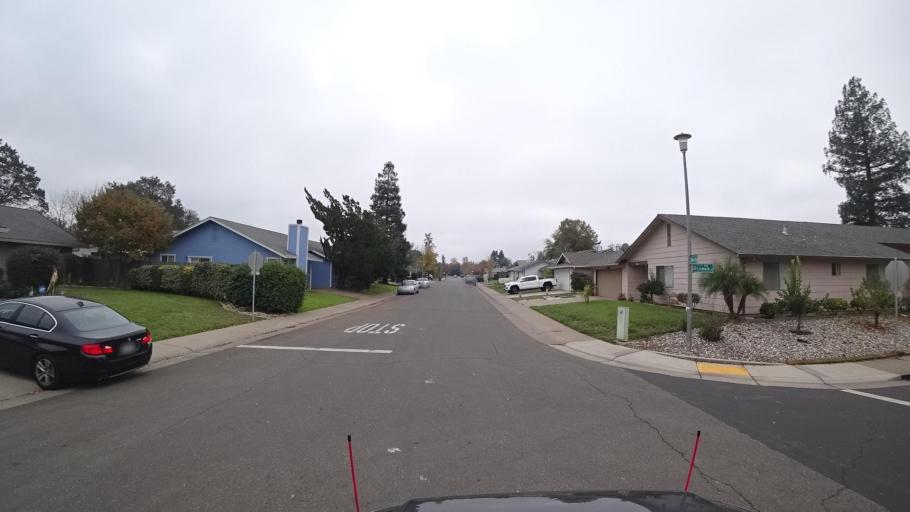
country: US
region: California
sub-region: Sacramento County
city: Elk Grove
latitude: 38.3976
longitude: -121.3618
